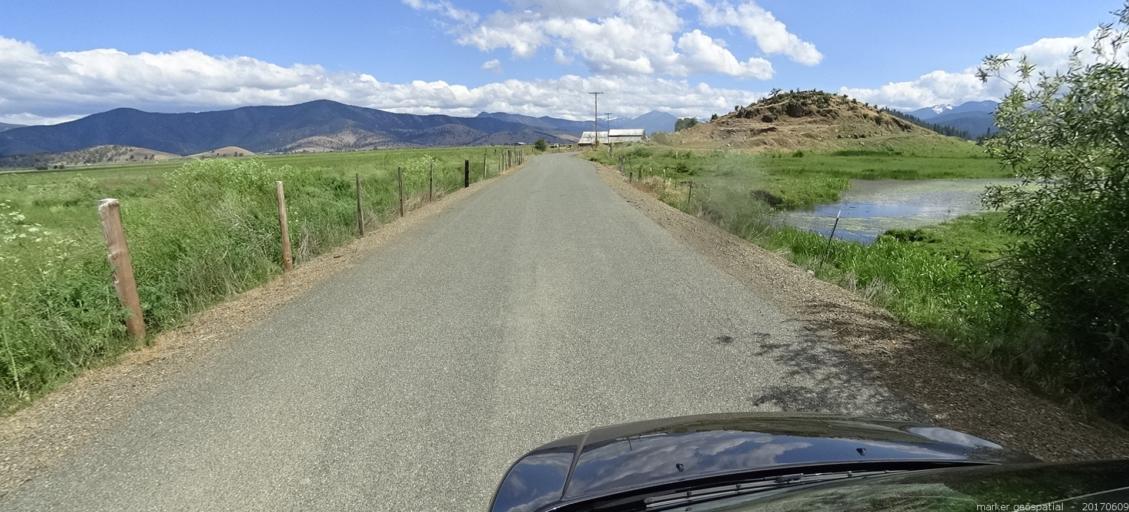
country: US
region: California
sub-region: Siskiyou County
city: Yreka
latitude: 41.4935
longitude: -122.8740
